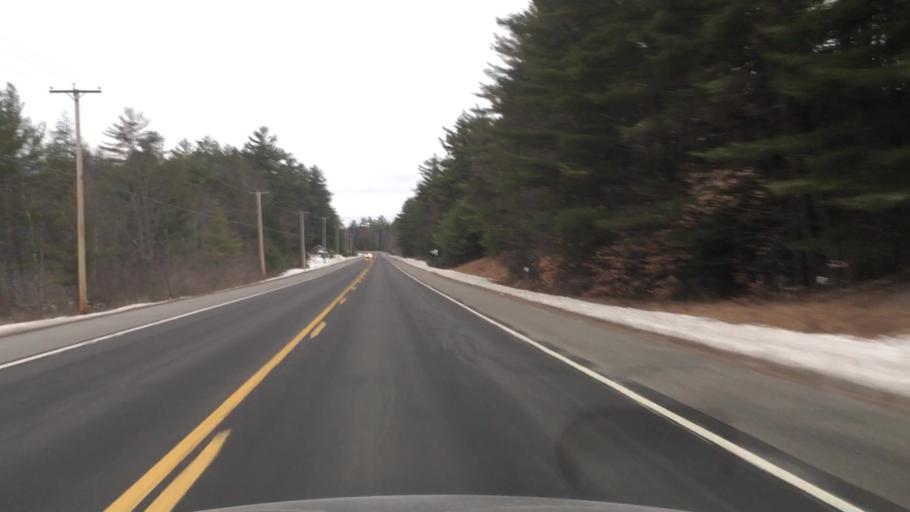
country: US
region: New Hampshire
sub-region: Merrimack County
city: Henniker
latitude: 43.2130
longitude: -71.8676
